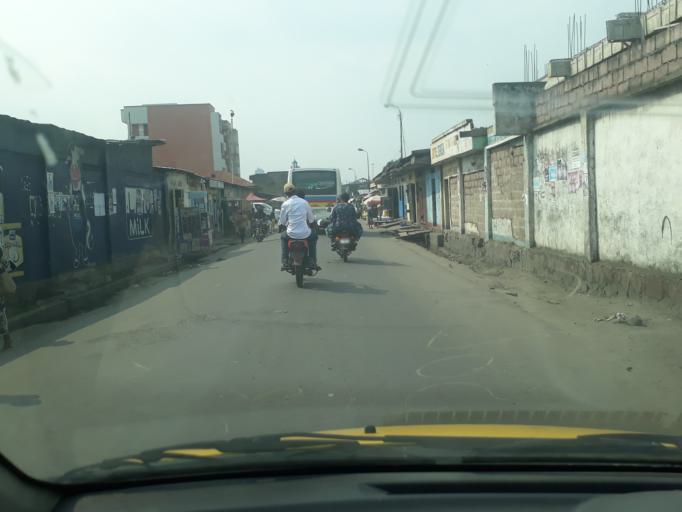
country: CD
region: Kinshasa
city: Kinshasa
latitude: -4.3181
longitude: 15.3201
